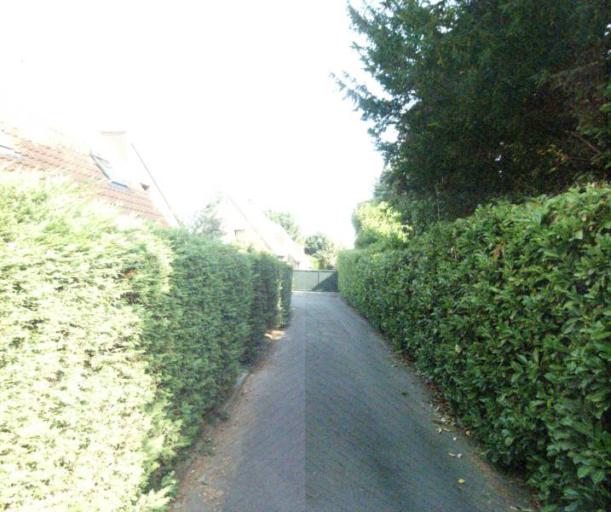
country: FR
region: Nord-Pas-de-Calais
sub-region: Departement du Nord
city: Mouvaux
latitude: 50.7091
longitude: 3.1374
